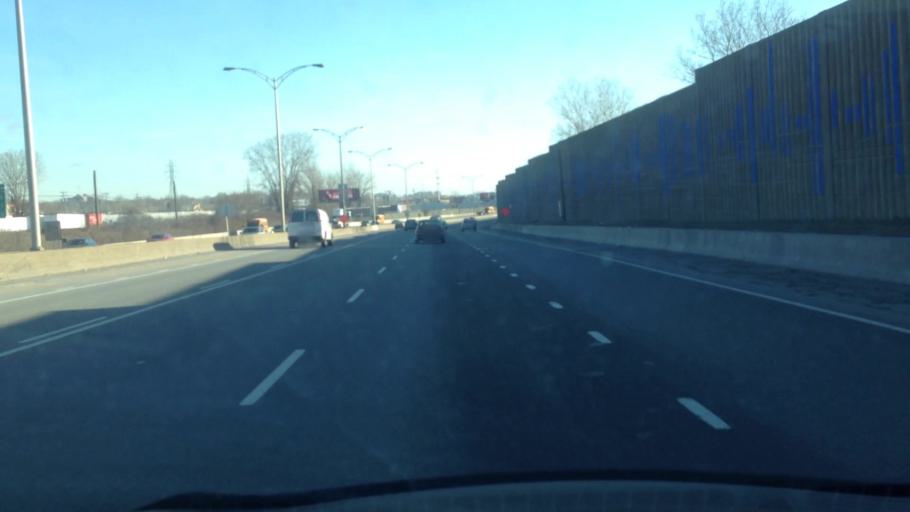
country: CA
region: Quebec
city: Cote-Saint-Luc
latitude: 45.4471
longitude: -73.6745
